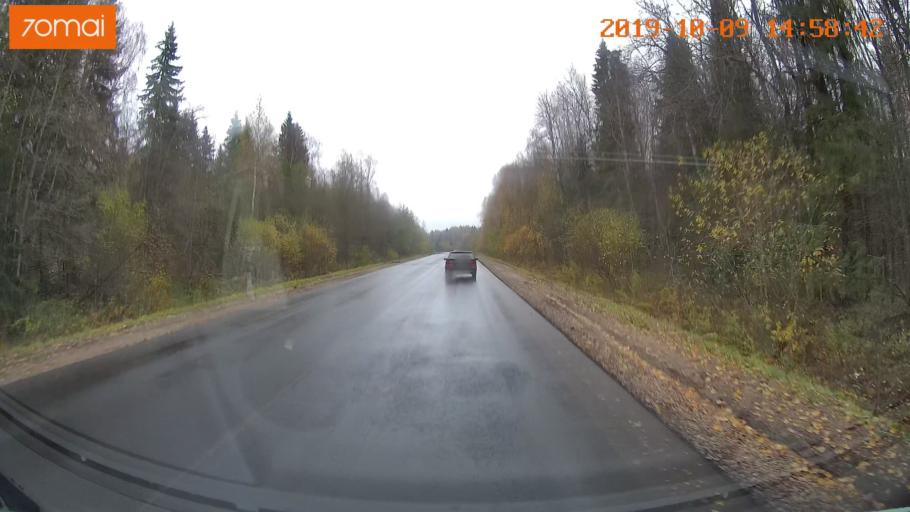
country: RU
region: Kostroma
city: Chistyye Bory
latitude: 58.3249
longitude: 41.6572
